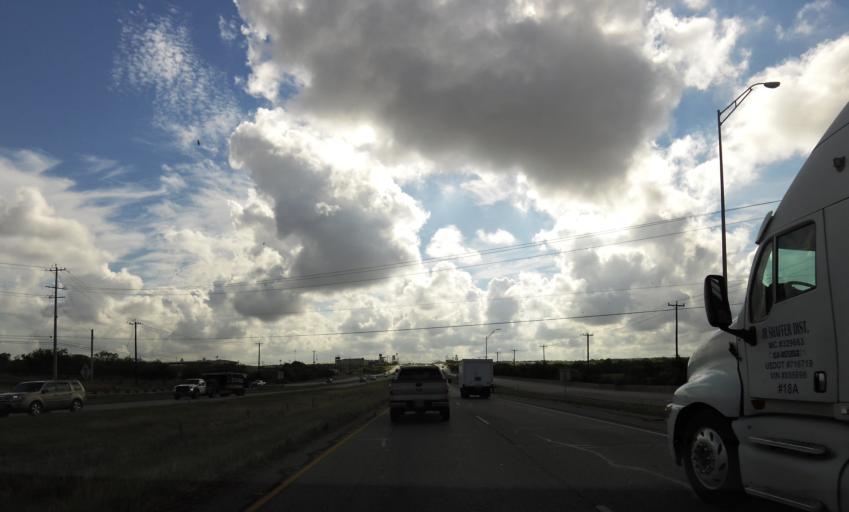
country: US
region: Texas
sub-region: Bexar County
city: Kirby
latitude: 29.4409
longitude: -98.3736
